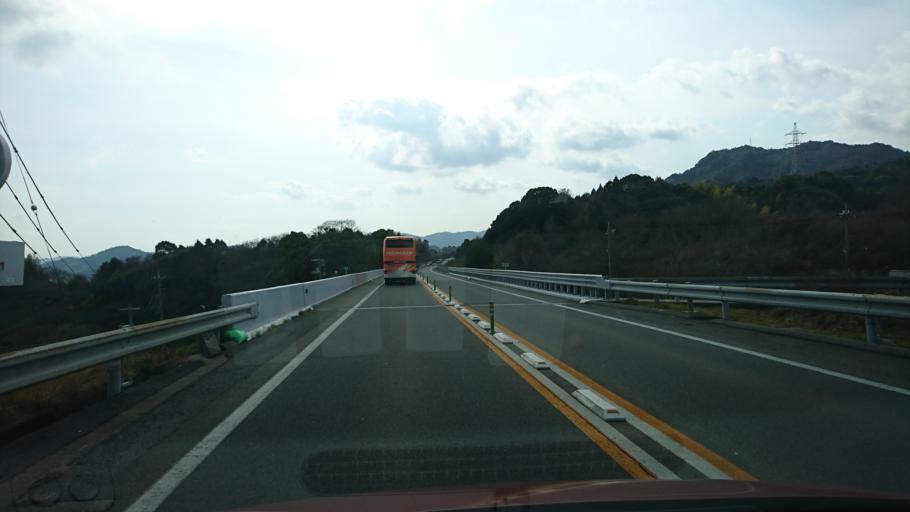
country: JP
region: Hiroshima
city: Innoshima
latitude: 34.2373
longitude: 133.0481
